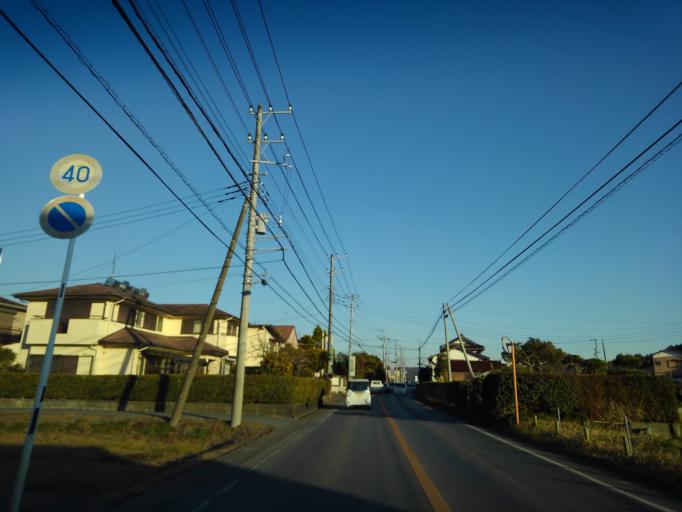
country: JP
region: Chiba
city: Kimitsu
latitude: 35.3063
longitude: 139.9539
